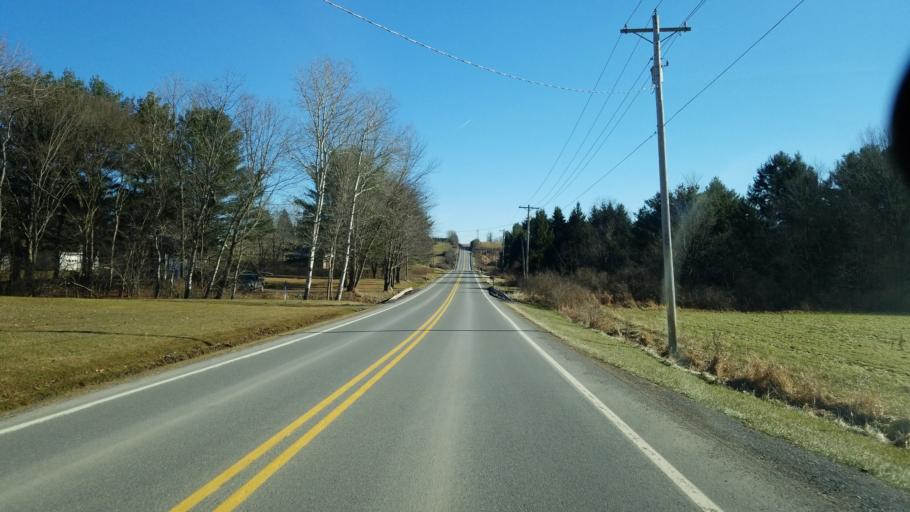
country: US
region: Pennsylvania
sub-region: Jefferson County
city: Falls Creek
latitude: 41.1822
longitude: -78.8721
